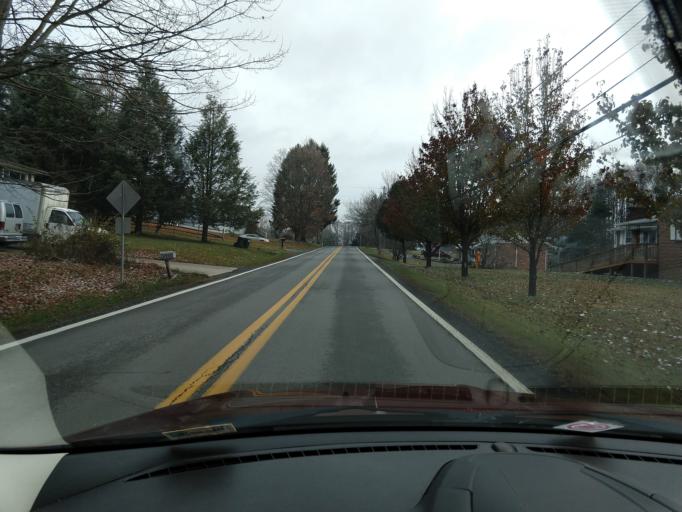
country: US
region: West Virginia
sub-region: Nicholas County
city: Craigsville
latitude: 38.2002
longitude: -80.6886
